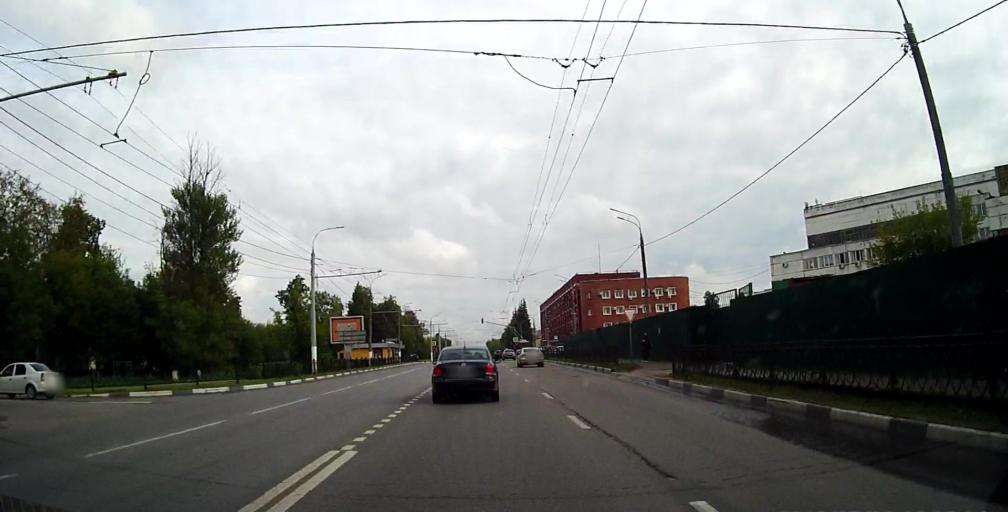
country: RU
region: Moskovskaya
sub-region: Podol'skiy Rayon
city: Podol'sk
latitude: 55.4206
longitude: 37.5688
